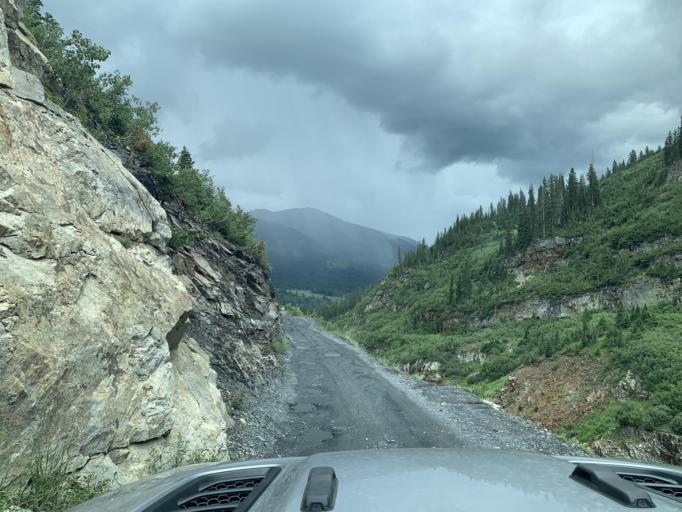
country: US
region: Colorado
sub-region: Gunnison County
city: Crested Butte
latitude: 39.0057
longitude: -107.0359
